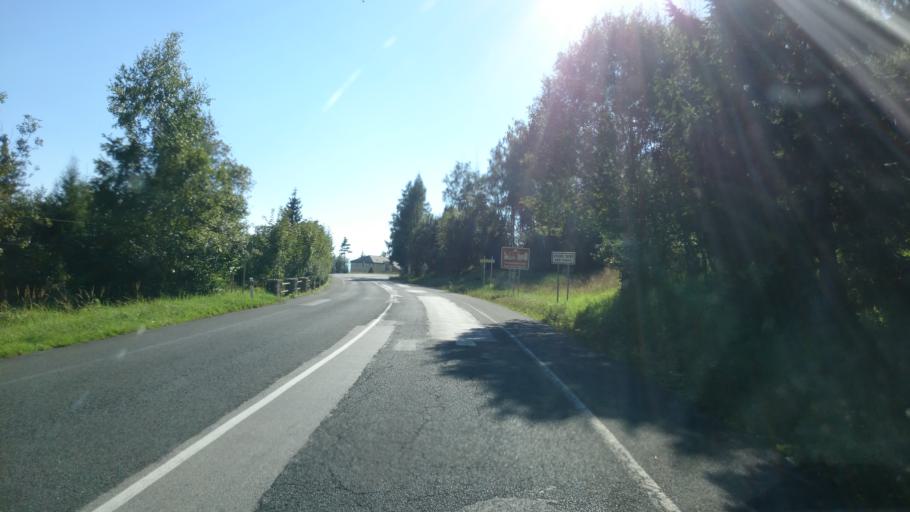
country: SK
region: Presovsky
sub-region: Okres Poprad
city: Vysoke Tatry
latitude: 49.1442
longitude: 20.2432
